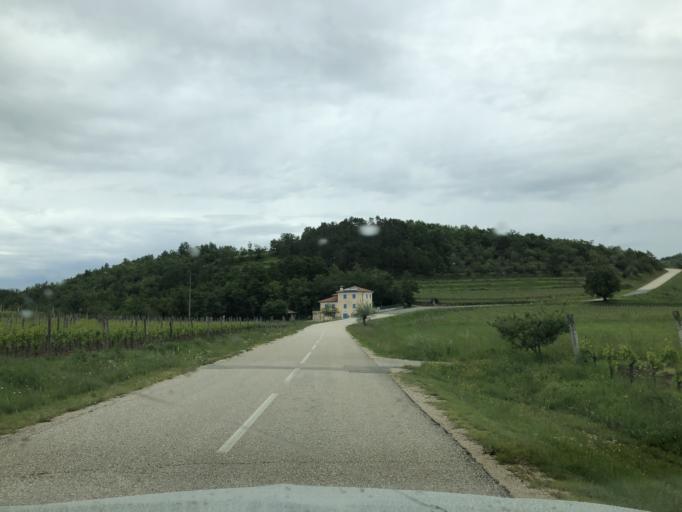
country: HR
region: Istarska
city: Buje
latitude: 45.4315
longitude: 13.6987
